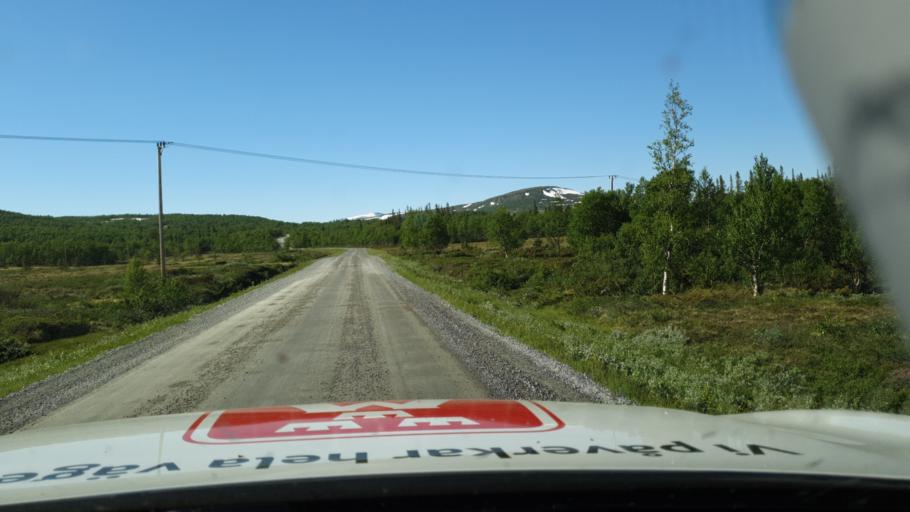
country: SE
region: Jaemtland
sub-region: Are Kommun
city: Are
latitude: 62.8829
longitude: 12.7258
